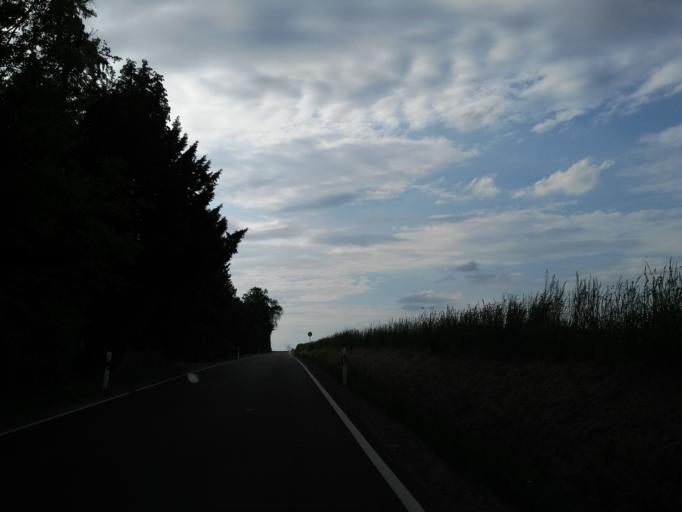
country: DE
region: Baden-Wuerttemberg
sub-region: Regierungsbezirk Stuttgart
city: Oberstenfeld
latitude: 49.0052
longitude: 9.3430
